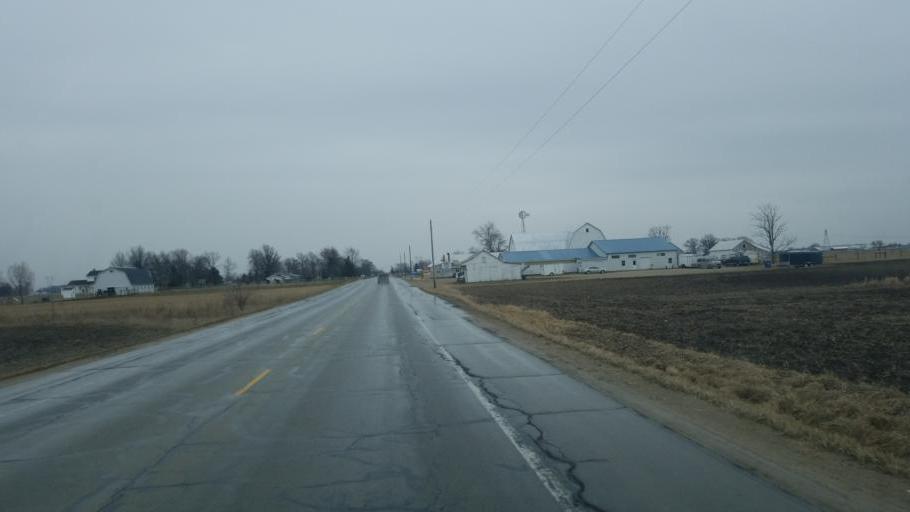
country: US
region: Indiana
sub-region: Adams County
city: Berne
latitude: 40.7153
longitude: -84.9559
